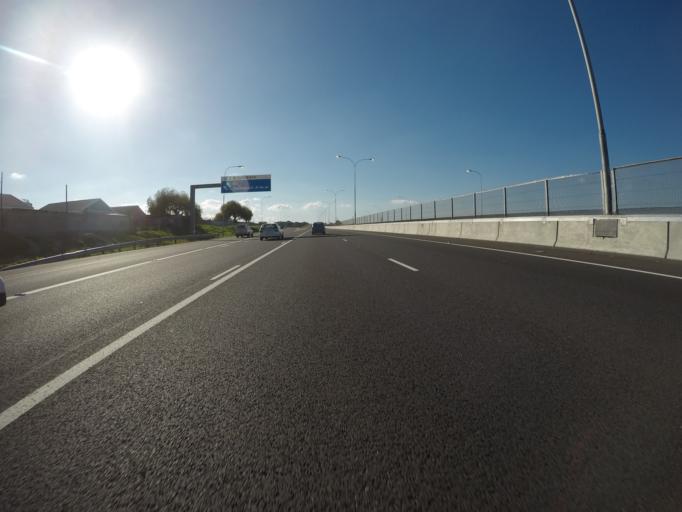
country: ZA
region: Western Cape
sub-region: City of Cape Town
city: Kraaifontein
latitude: -33.9604
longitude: 18.6561
